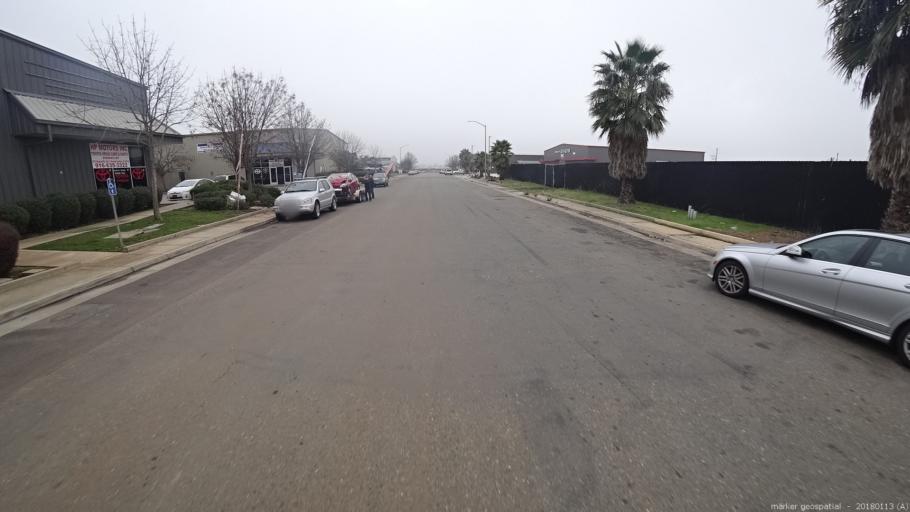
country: US
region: California
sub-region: Sacramento County
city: Rancho Cordova
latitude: 38.5659
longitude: -121.2525
